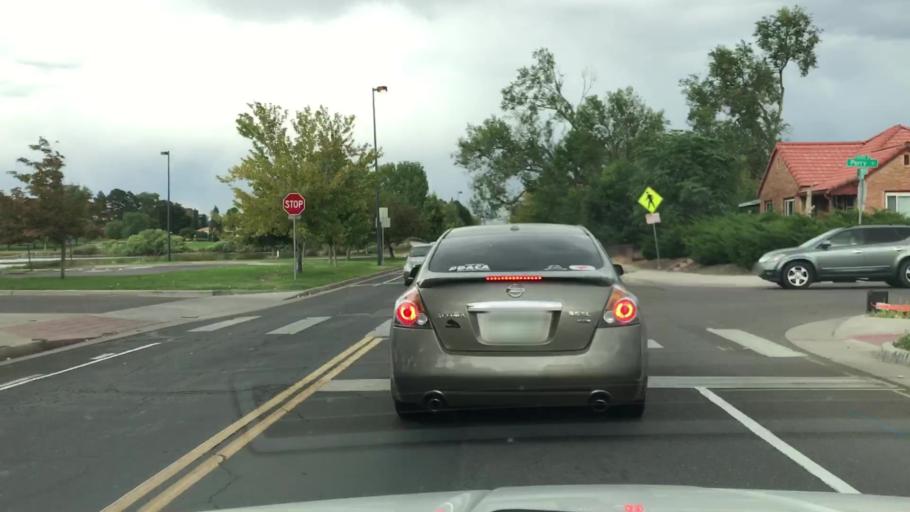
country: US
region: Colorado
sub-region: Jefferson County
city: Edgewater
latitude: 39.7439
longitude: -105.0398
